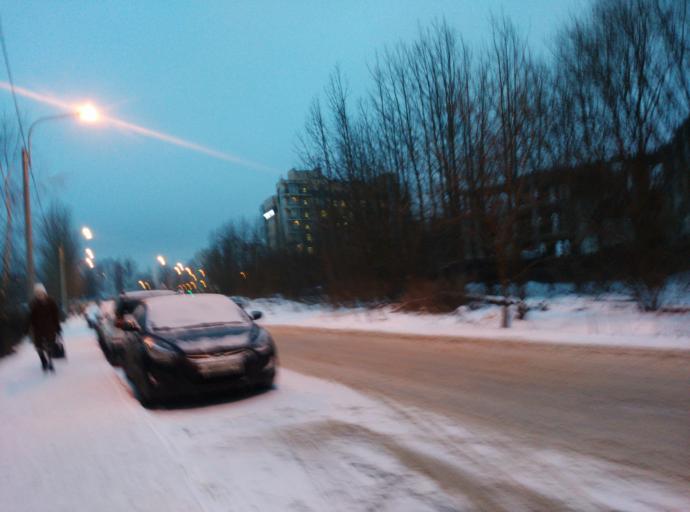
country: RU
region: St.-Petersburg
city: Kolomyagi
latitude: 60.0216
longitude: 30.2984
